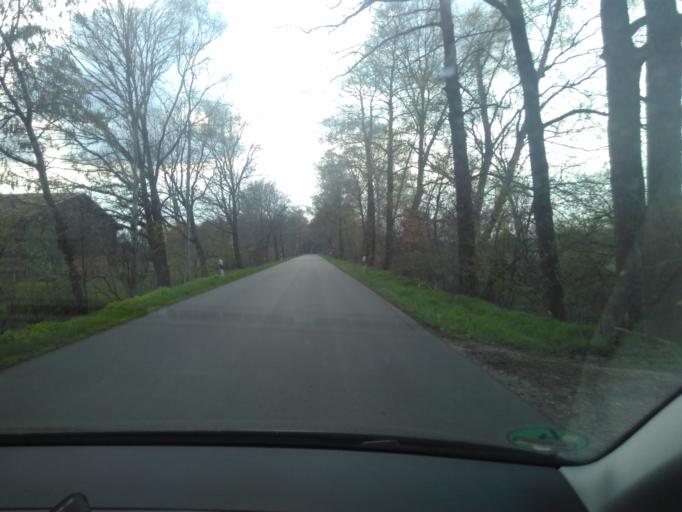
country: DE
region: Lower Saxony
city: Adelheidsdorf
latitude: 52.5507
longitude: 10.0146
